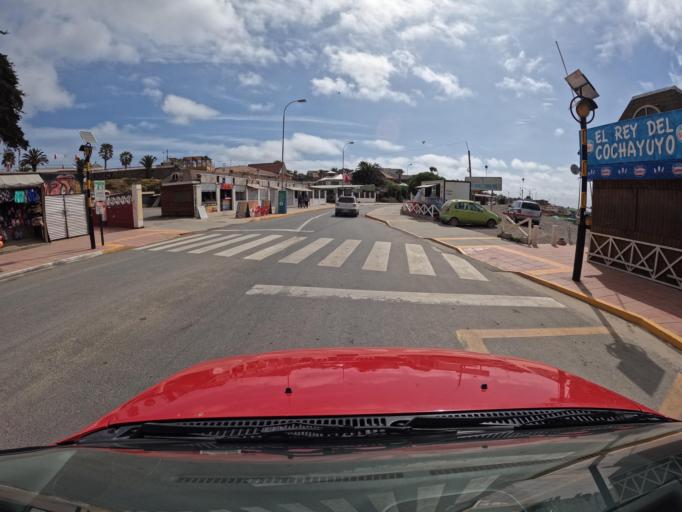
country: CL
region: O'Higgins
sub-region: Provincia de Colchagua
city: Santa Cruz
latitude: -34.3848
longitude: -72.0113
